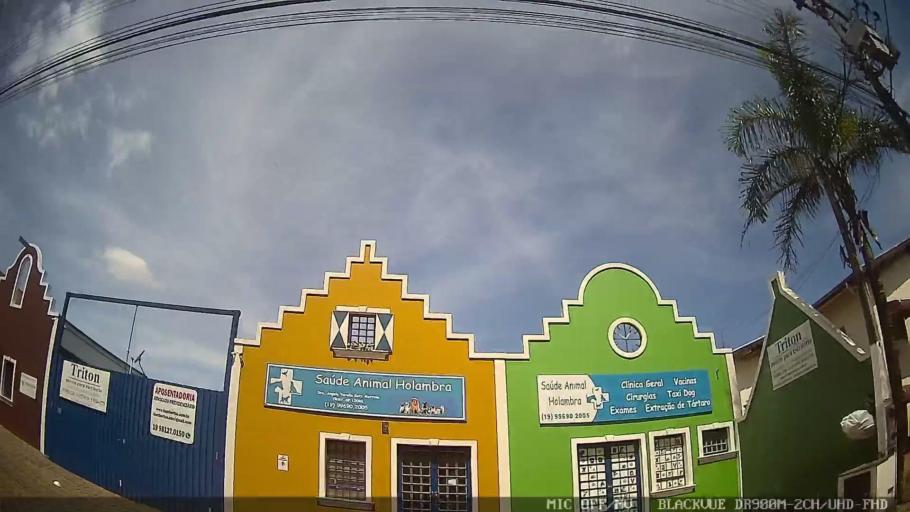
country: BR
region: Sao Paulo
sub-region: Jaguariuna
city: Jaguariuna
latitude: -22.6154
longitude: -47.0615
